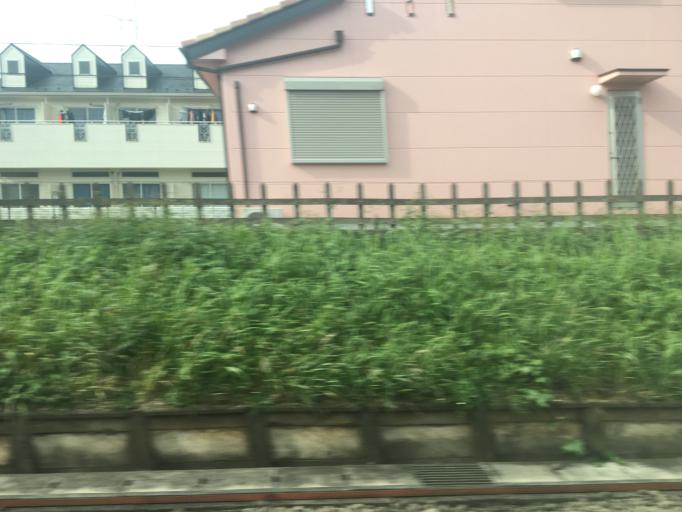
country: JP
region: Saitama
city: Sayama
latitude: 35.8476
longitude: 139.4167
